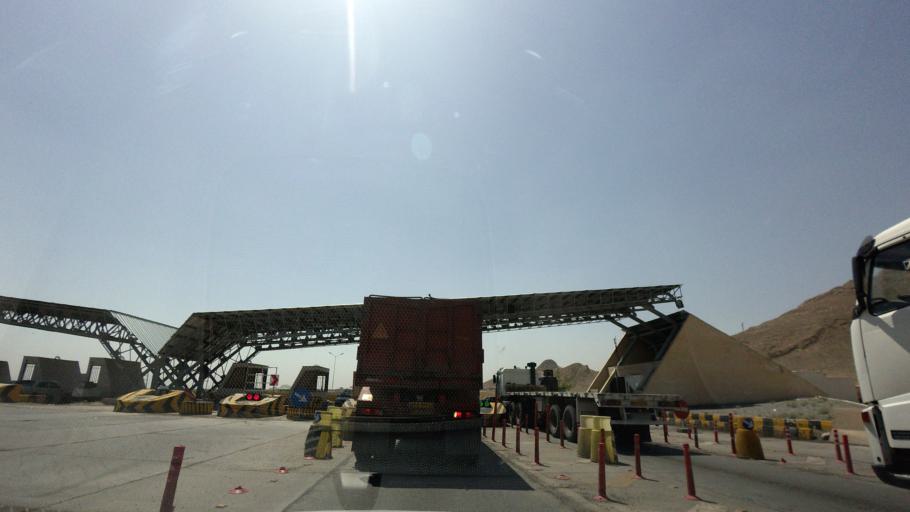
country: IR
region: Isfahan
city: Najafabad
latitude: 32.5825
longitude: 51.2878
